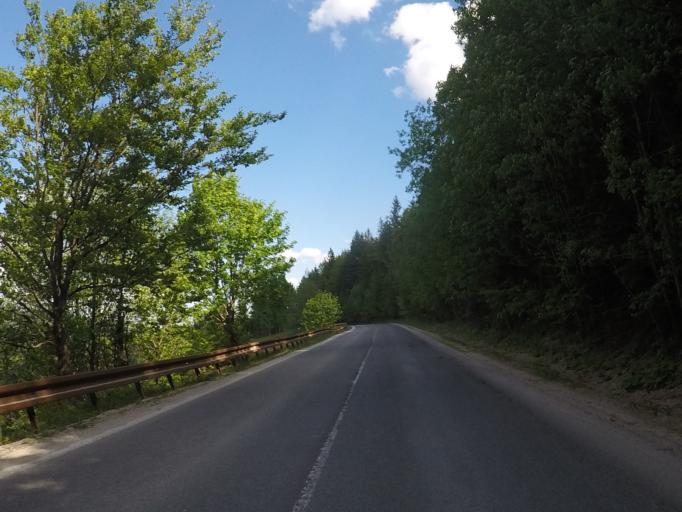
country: SK
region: Kosicky
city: Dobsina
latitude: 48.8541
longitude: 20.3593
